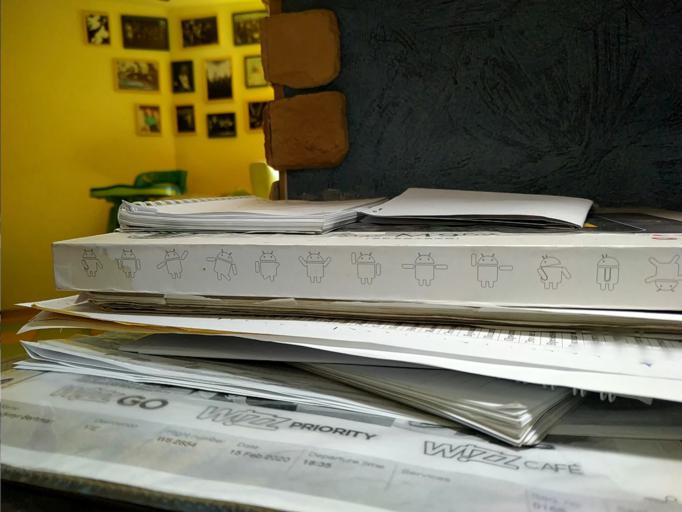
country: RU
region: Novgorod
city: Sol'tsy
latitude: 58.0482
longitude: 30.1829
